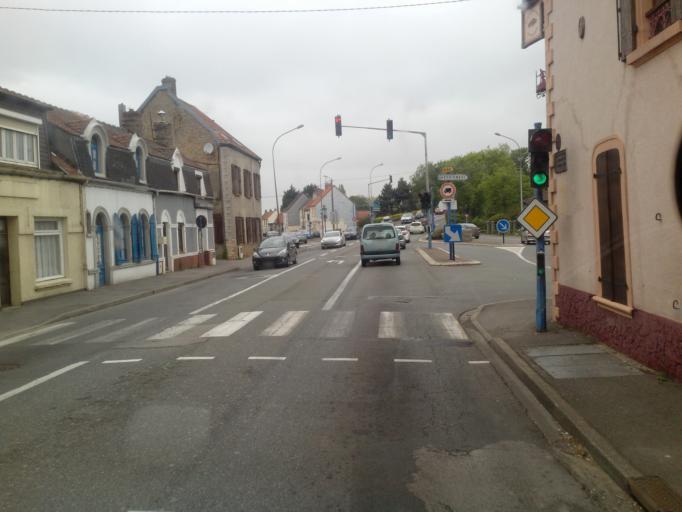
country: FR
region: Nord-Pas-de-Calais
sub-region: Departement du Pas-de-Calais
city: Saint-Etienne-au-Mont
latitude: 50.6778
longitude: 1.6341
